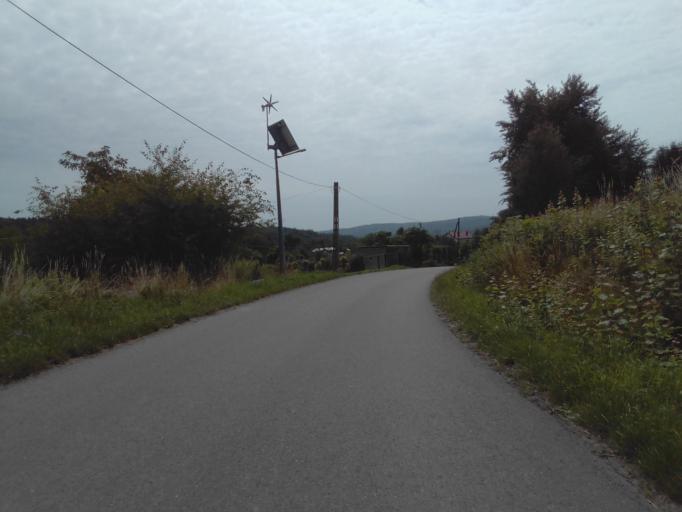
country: PL
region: Subcarpathian Voivodeship
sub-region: Powiat jasielski
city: Kolaczyce
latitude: 49.8181
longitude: 21.4984
